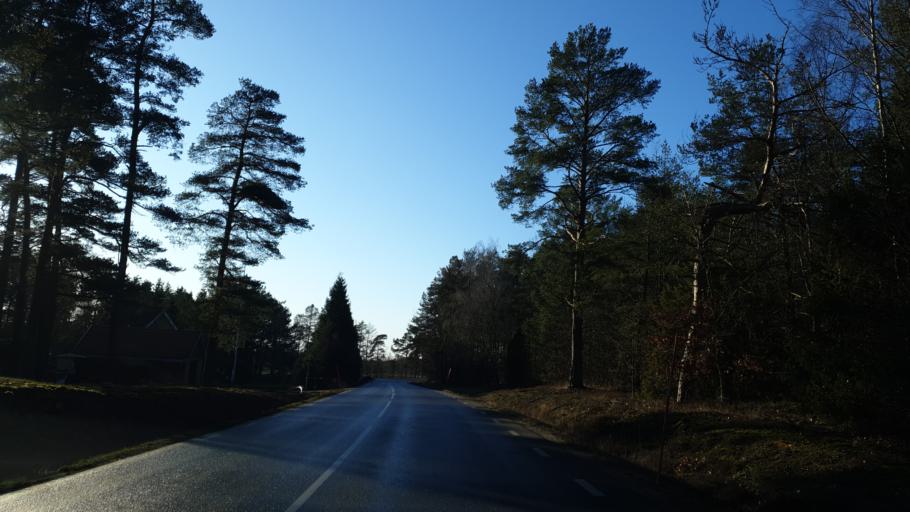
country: SE
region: Blekinge
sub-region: Ronneby Kommun
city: Kallinge
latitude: 56.1947
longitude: 15.3670
